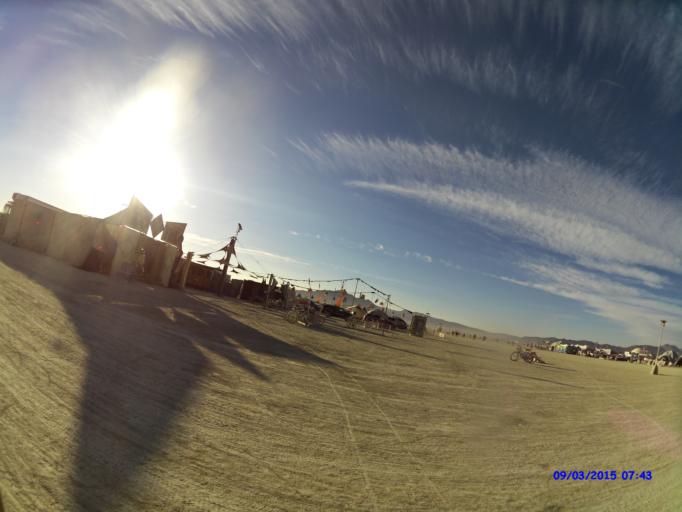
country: US
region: Nevada
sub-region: Pershing County
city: Lovelock
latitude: 40.7923
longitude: -119.2138
